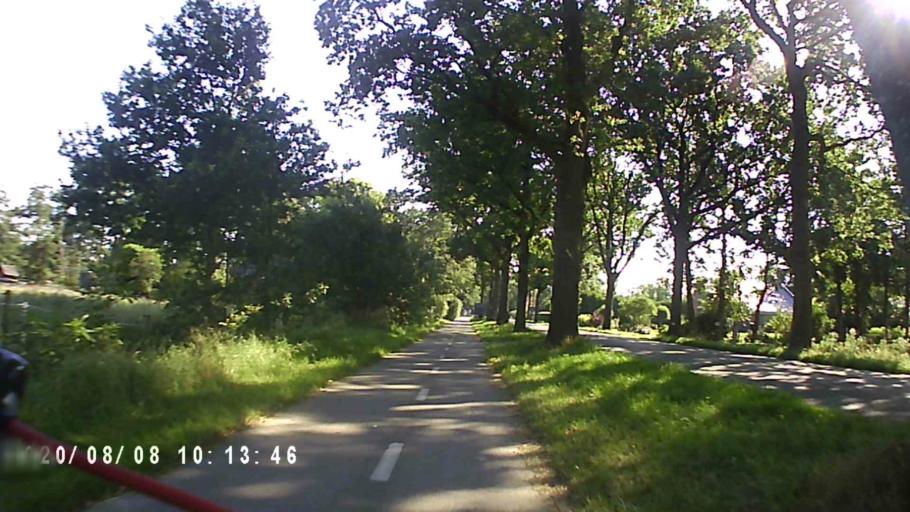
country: NL
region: Groningen
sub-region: Gemeente Leek
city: Leek
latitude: 53.1271
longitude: 6.3906
